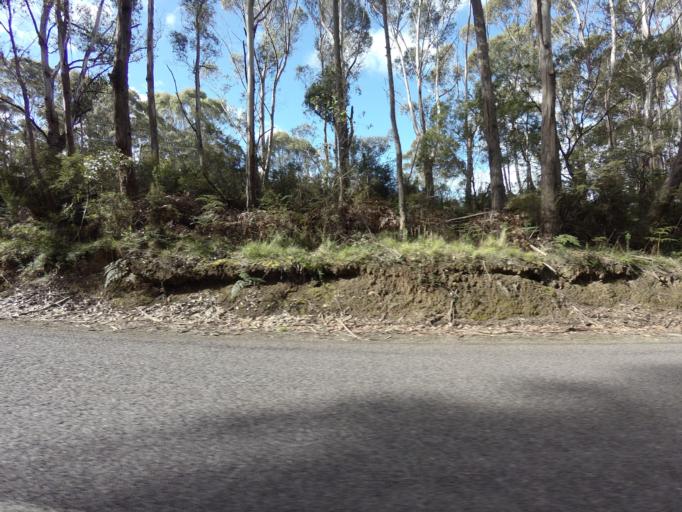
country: AU
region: Tasmania
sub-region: Huon Valley
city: Geeveston
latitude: -43.1993
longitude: 146.9603
